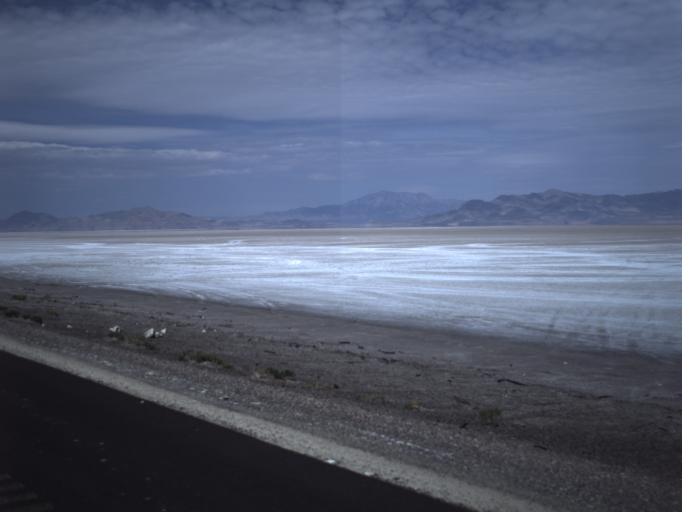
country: US
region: Utah
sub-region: Tooele County
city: Wendover
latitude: 40.7352
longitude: -113.6505
